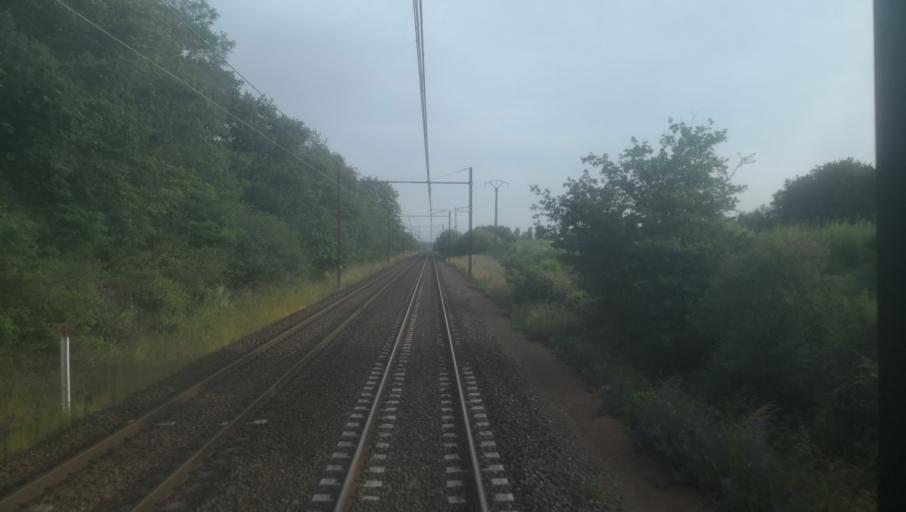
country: FR
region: Centre
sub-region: Departement du Loiret
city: La Ferte-Saint-Aubin
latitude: 47.7040
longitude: 1.9374
